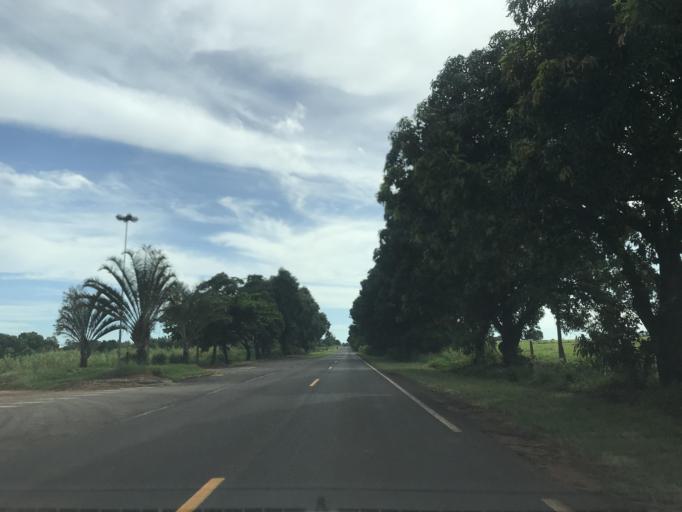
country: BR
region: Parana
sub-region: Terra Rica
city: Terra Rica
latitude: -22.7598
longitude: -52.6335
